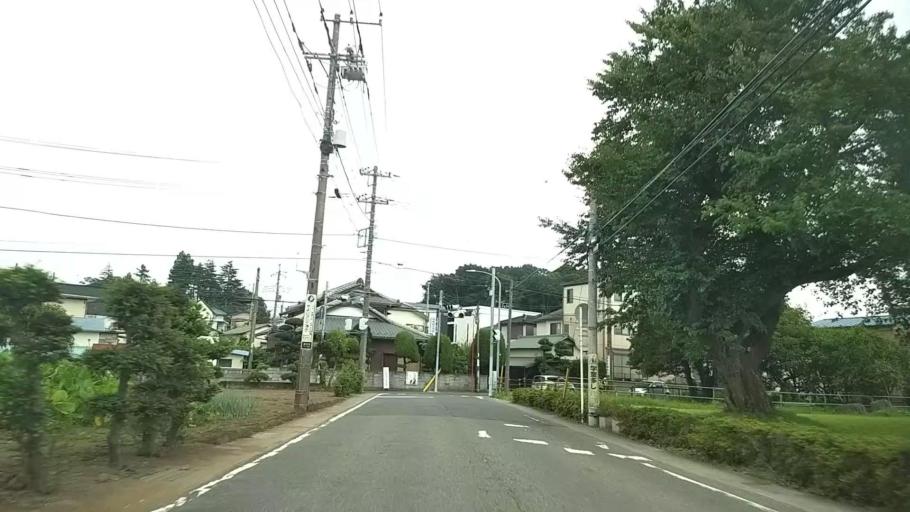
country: JP
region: Kanagawa
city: Zama
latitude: 35.4547
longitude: 139.3985
